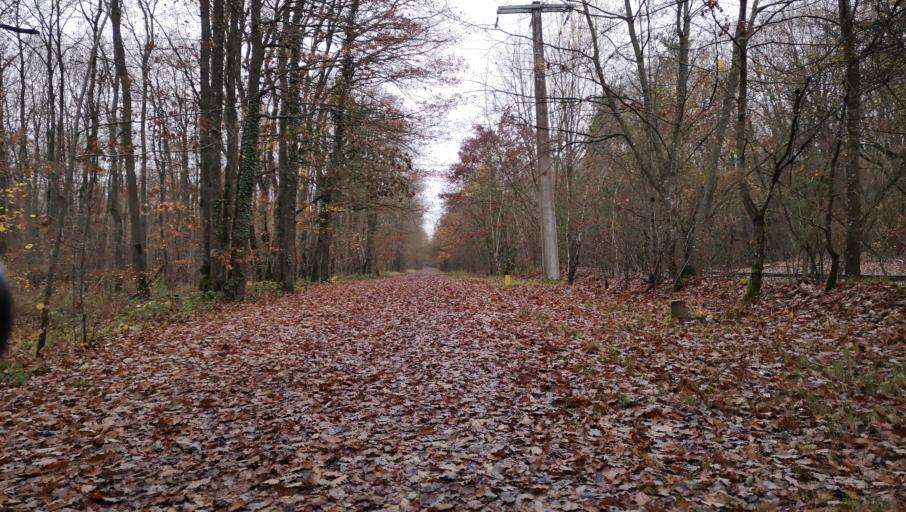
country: FR
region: Centre
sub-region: Departement du Loiret
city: Chanteau
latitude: 47.9444
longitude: 1.9817
